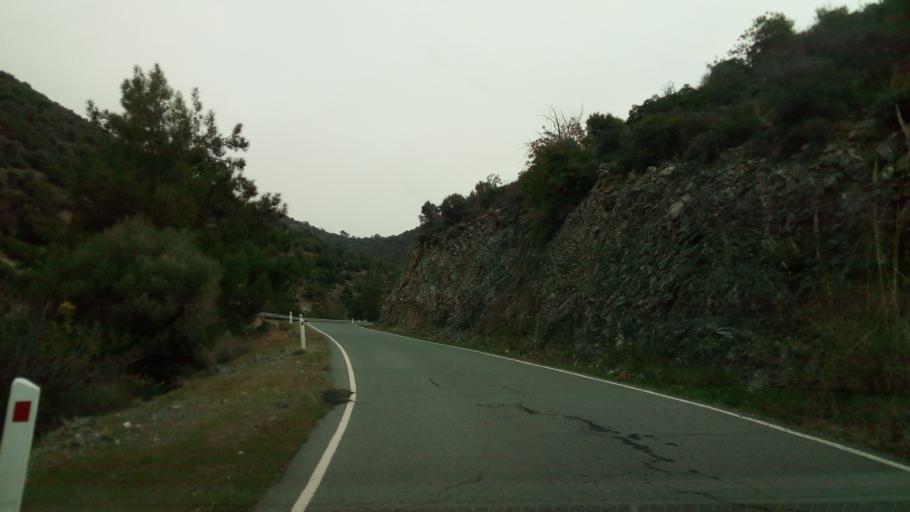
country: CY
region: Limassol
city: Mouttagiaka
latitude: 34.7779
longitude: 33.0857
